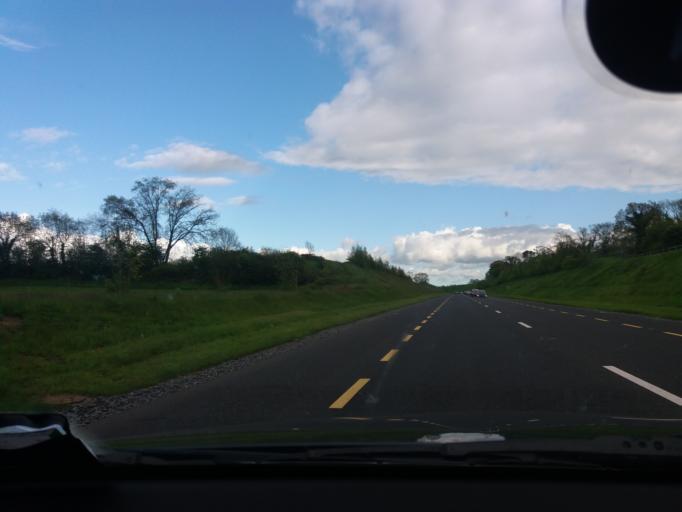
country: IE
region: Leinster
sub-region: Kilkenny
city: Kilkenny
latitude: 52.6509
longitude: -7.1944
